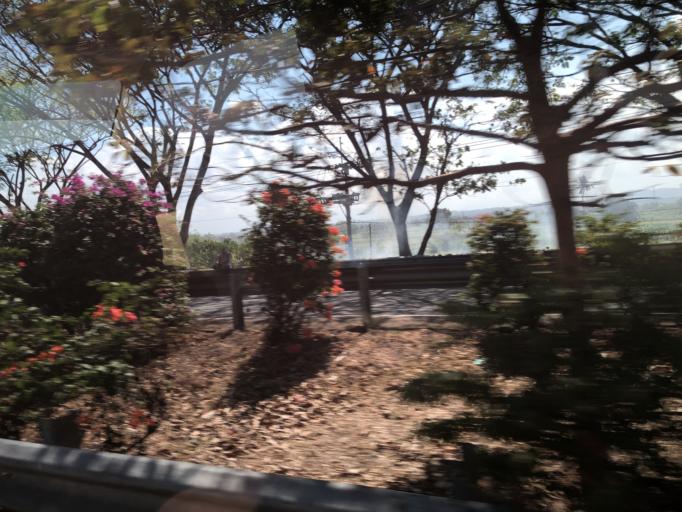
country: ID
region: Bali
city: Semarapura
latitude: -8.5689
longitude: 115.4087
